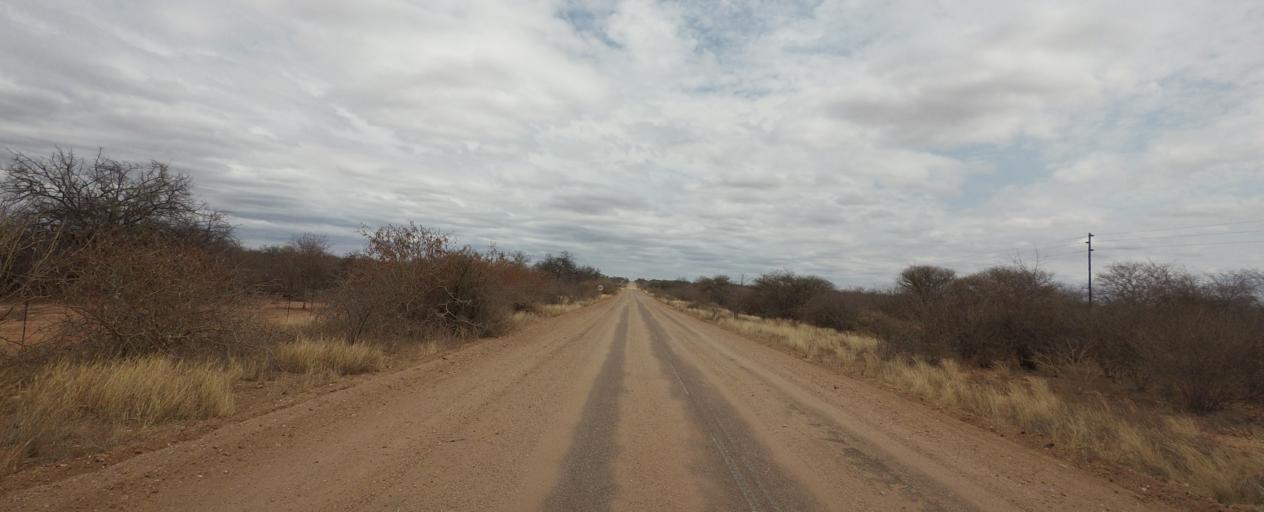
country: BW
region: Central
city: Mathathane
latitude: -22.6736
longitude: 28.6766
